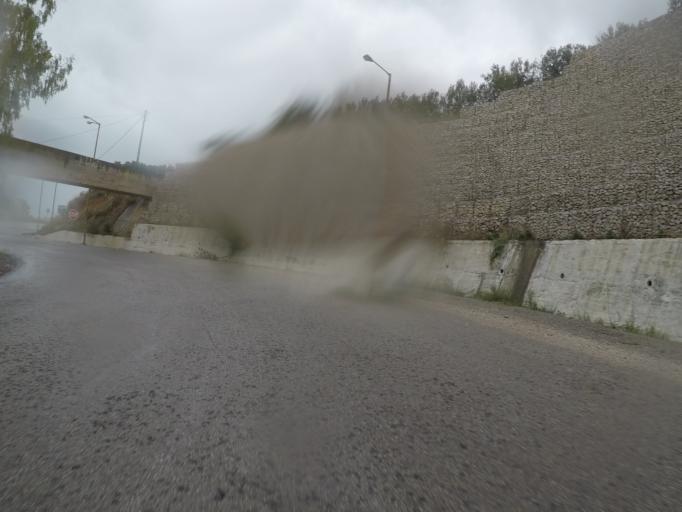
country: GR
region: Peloponnese
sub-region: Nomos Korinthias
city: Arkhaia Korinthos
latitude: 37.9136
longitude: 22.8876
